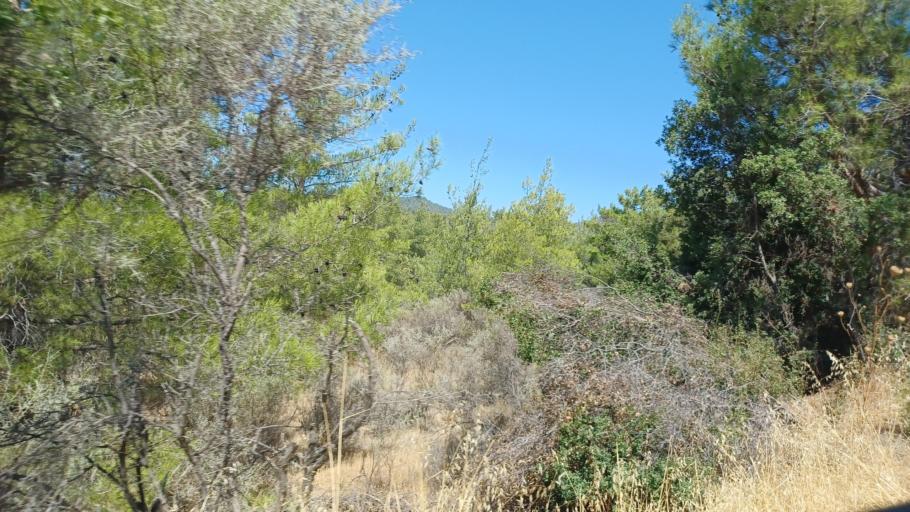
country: CY
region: Pafos
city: Mesogi
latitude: 34.9334
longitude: 32.6309
